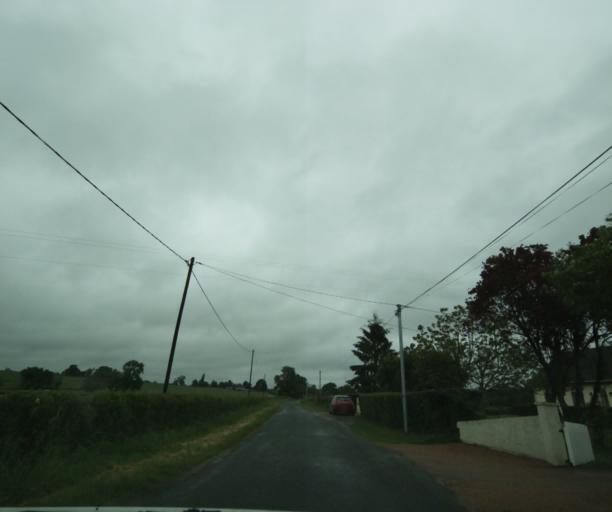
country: FR
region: Bourgogne
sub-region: Departement de Saone-et-Loire
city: Palinges
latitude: 46.5711
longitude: 4.2148
